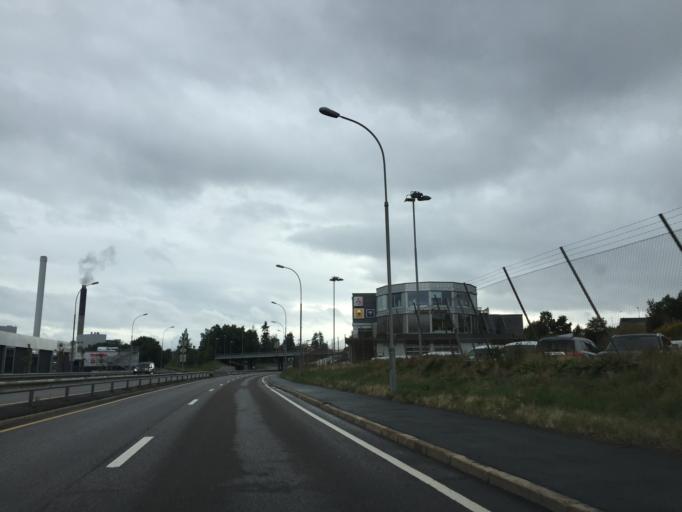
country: NO
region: Oslo
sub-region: Oslo
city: Oslo
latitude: 59.9348
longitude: 10.8313
